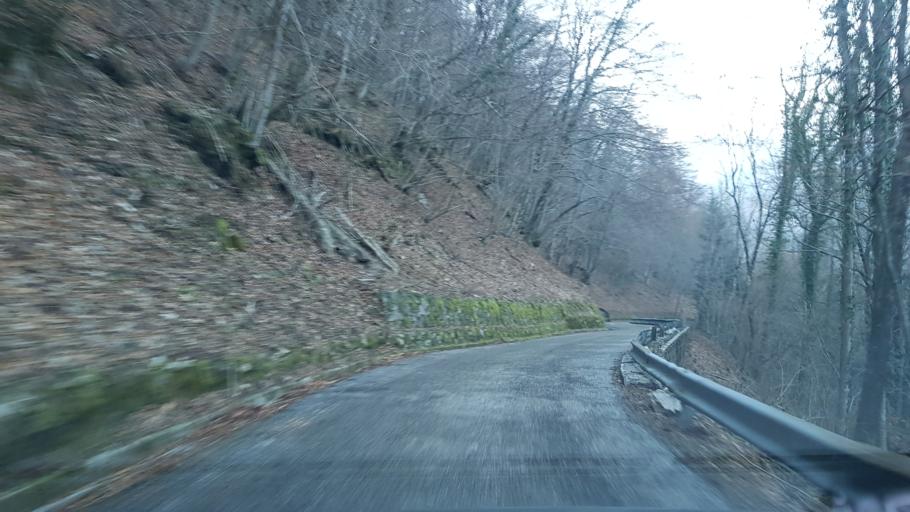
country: IT
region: Friuli Venezia Giulia
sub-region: Provincia di Udine
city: Taipana
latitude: 46.2435
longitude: 13.4033
